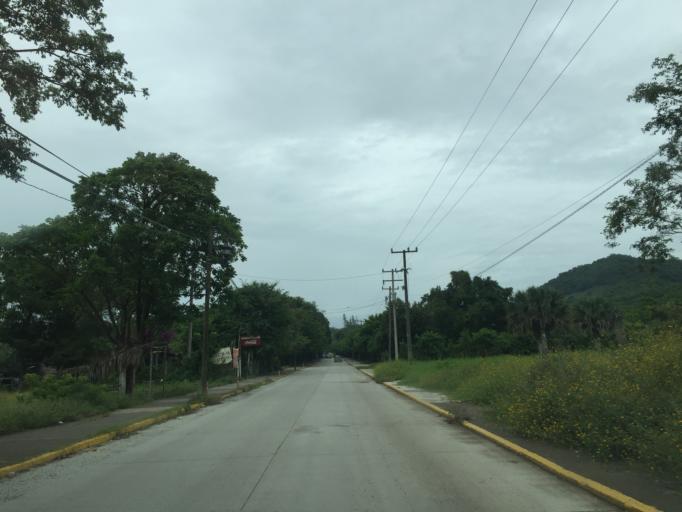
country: MX
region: Veracruz
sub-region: Papantla
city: El Chote
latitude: 20.4374
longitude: -97.3790
